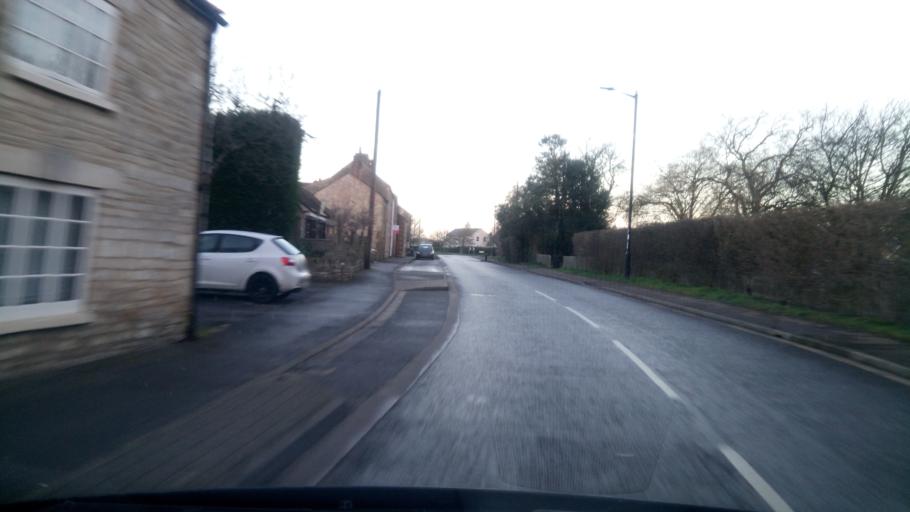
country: GB
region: England
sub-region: Peterborough
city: Castor
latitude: 52.5749
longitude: -0.3519
